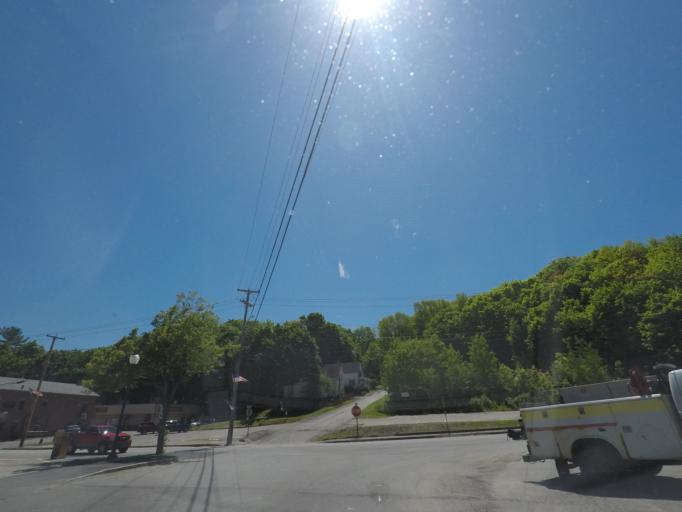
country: US
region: Maine
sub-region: Kennebec County
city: Gardiner
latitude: 44.2296
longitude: -69.7771
